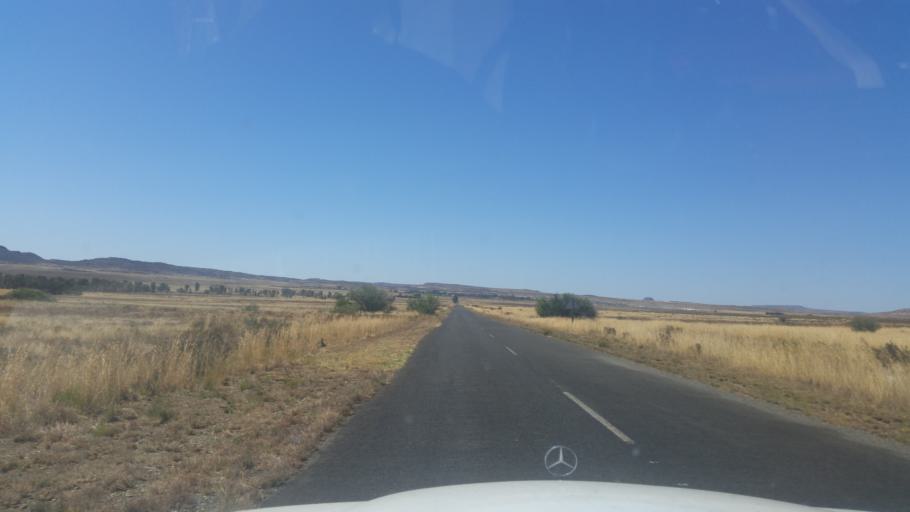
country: ZA
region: Eastern Cape
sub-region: Joe Gqabi District Municipality
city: Burgersdorp
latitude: -30.7474
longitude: 25.7625
